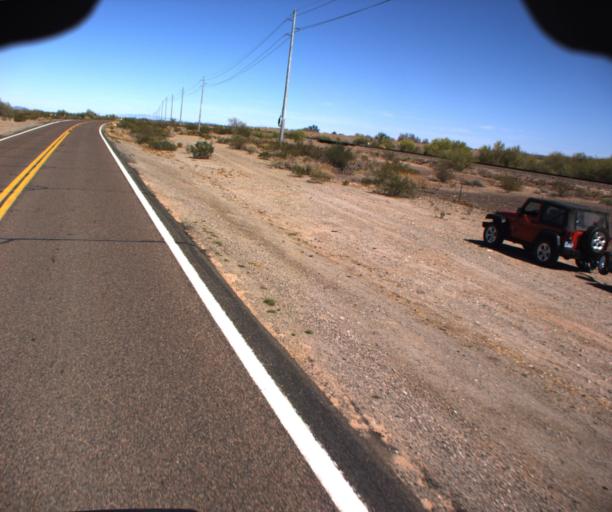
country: US
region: Arizona
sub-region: La Paz County
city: Salome
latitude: 33.7631
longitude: -113.7847
